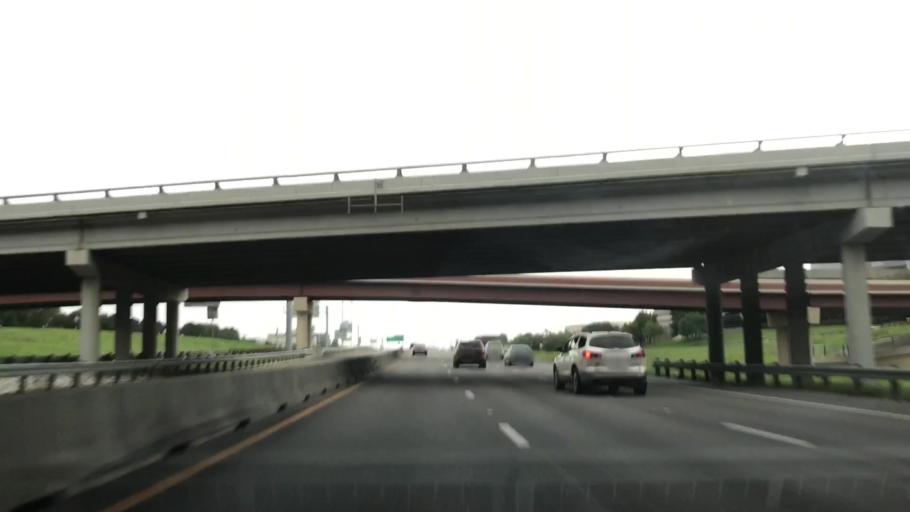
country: US
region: Texas
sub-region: Dallas County
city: Coppell
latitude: 32.8958
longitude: -96.9727
